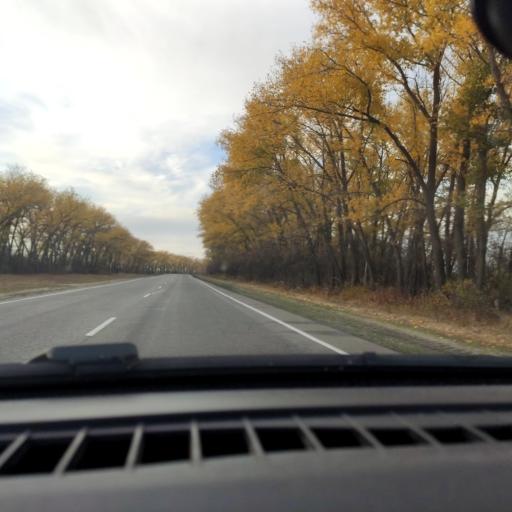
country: RU
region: Voronezj
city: Ostrogozhsk
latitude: 50.9711
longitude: 39.0009
